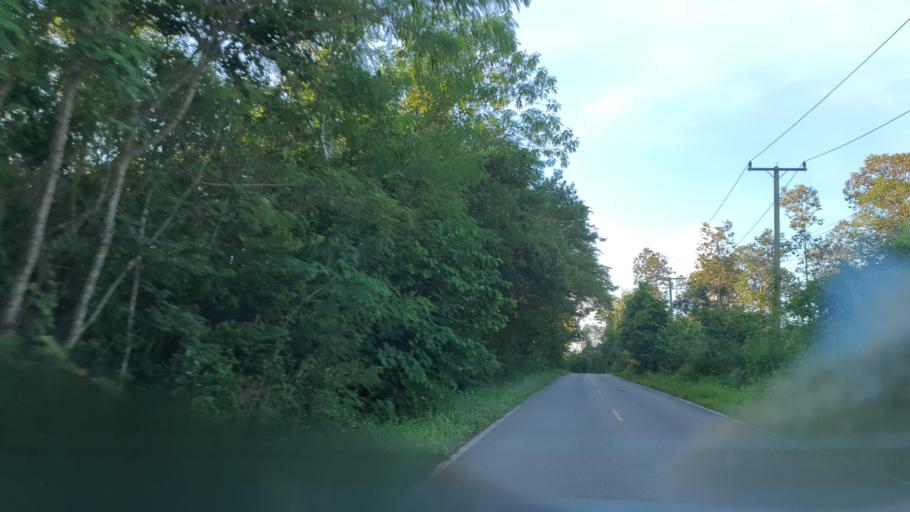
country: TH
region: Chiang Mai
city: Mae On
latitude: 18.8419
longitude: 99.2801
